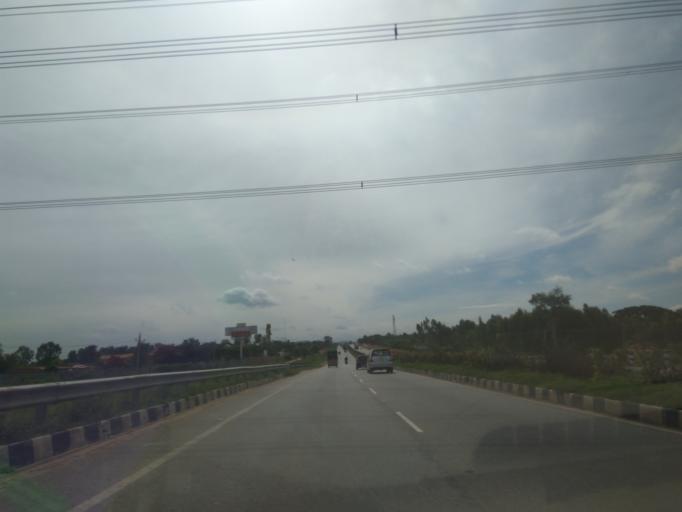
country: IN
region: Karnataka
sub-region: Bangalore Rural
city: Dasarahalli
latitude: 13.1333
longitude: 77.9496
